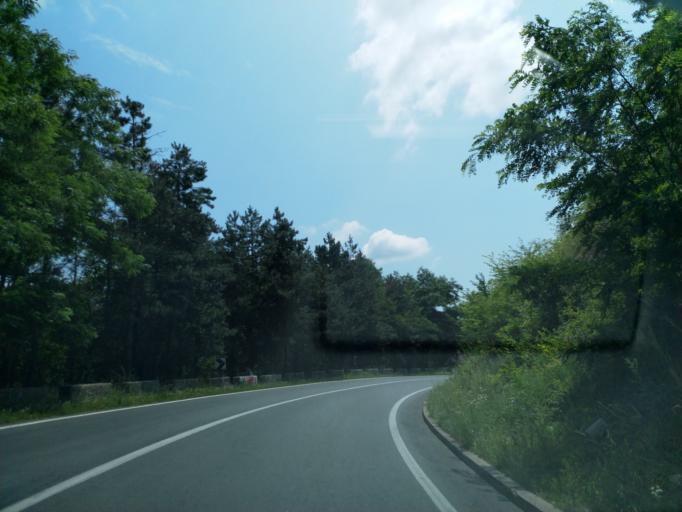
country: RS
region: Central Serbia
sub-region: Rasinski Okrug
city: Aleksandrovac
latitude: 43.4037
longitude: 21.1582
